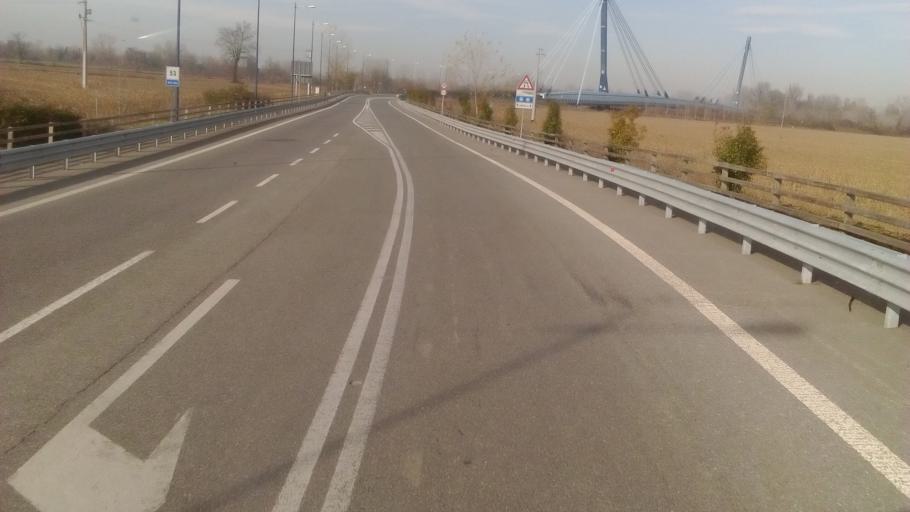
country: IT
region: Lombardy
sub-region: Provincia di Cremona
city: Gombito
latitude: 45.2493
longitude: 9.7025
